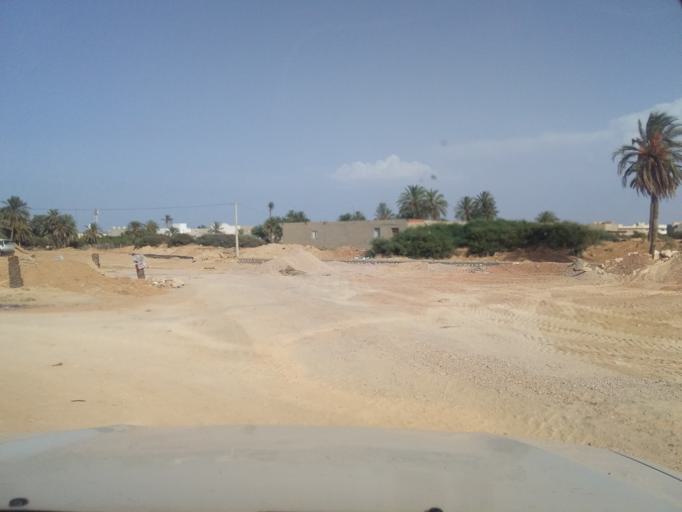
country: TN
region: Qabis
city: Matmata
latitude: 33.6152
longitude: 10.2811
